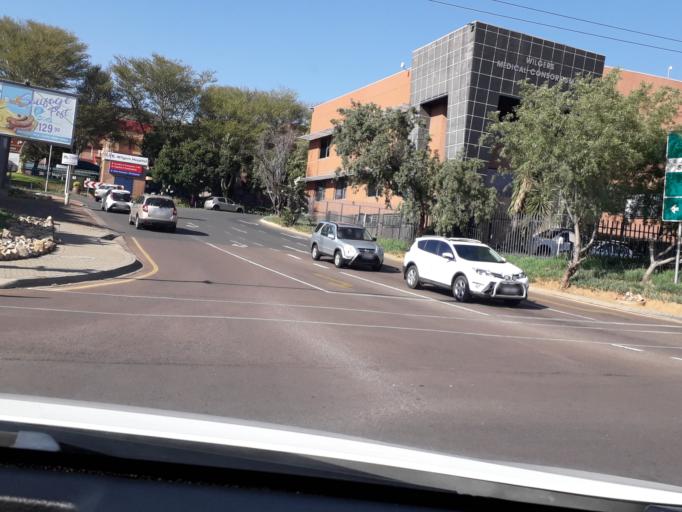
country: ZA
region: Gauteng
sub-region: City of Tshwane Metropolitan Municipality
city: Pretoria
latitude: -25.7670
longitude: 28.3212
